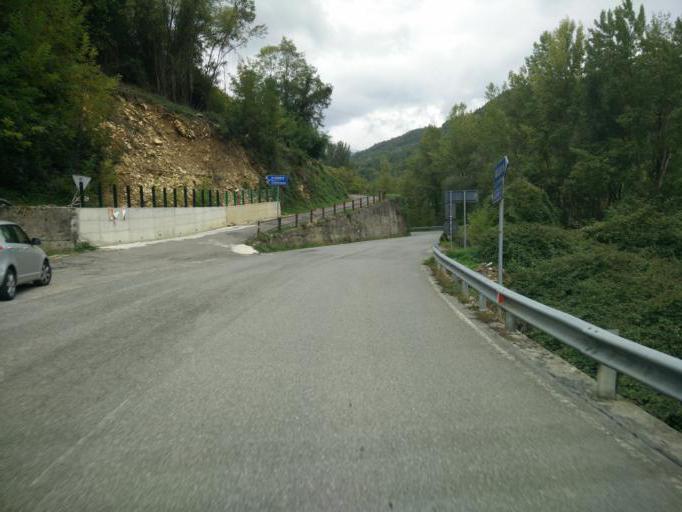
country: IT
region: Tuscany
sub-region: Provincia di Massa-Carrara
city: Fivizzano
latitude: 44.1973
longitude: 10.1245
